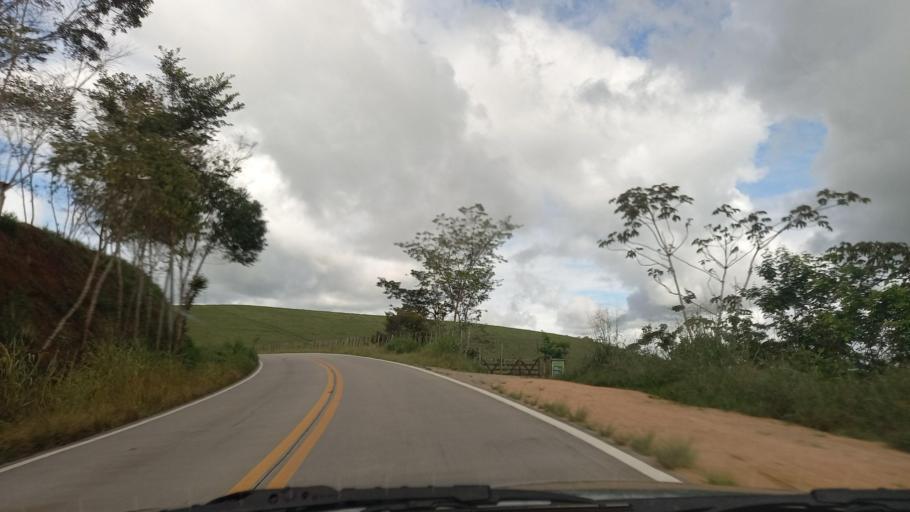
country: BR
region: Pernambuco
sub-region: Maraial
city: Maraial
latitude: -8.7866
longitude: -35.9062
